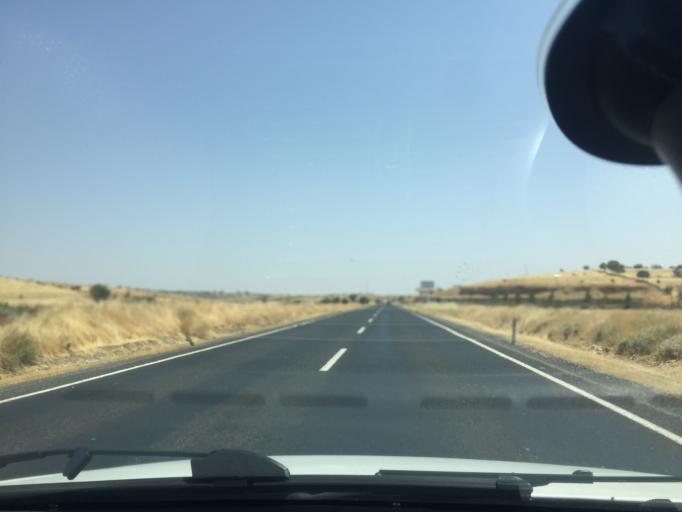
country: TR
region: Mardin
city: Kindirip
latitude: 37.4523
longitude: 41.2584
